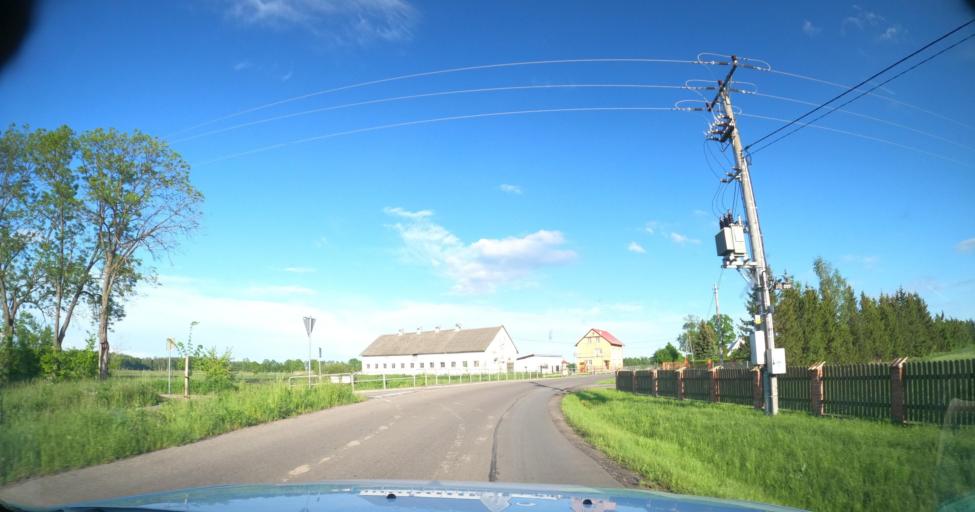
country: PL
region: Warmian-Masurian Voivodeship
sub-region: Powiat braniewski
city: Braniewo
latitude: 54.2726
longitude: 19.8080
